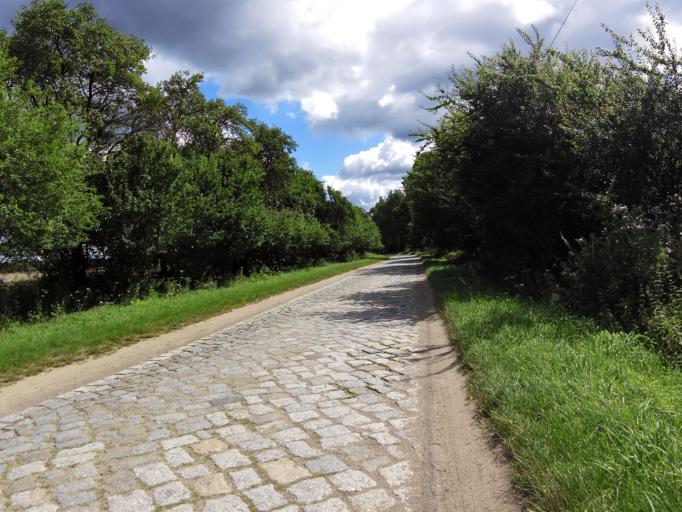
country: DE
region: Brandenburg
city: Lychen
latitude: 53.2688
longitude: 13.3512
